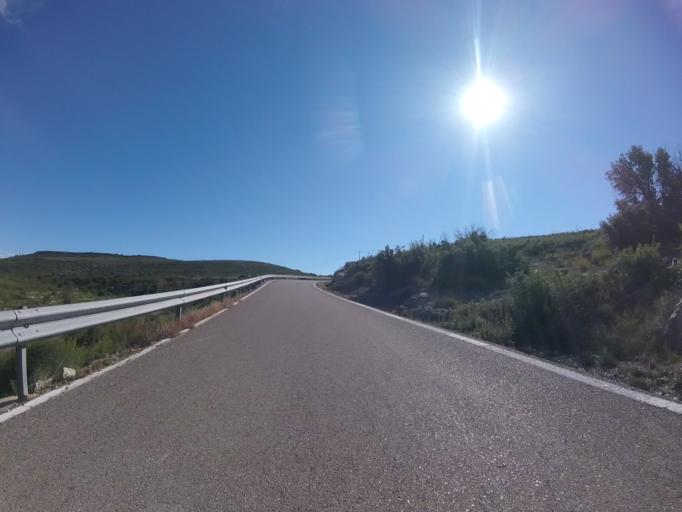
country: ES
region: Valencia
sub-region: Provincia de Castello
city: Albocasser
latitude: 40.3749
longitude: 0.0189
